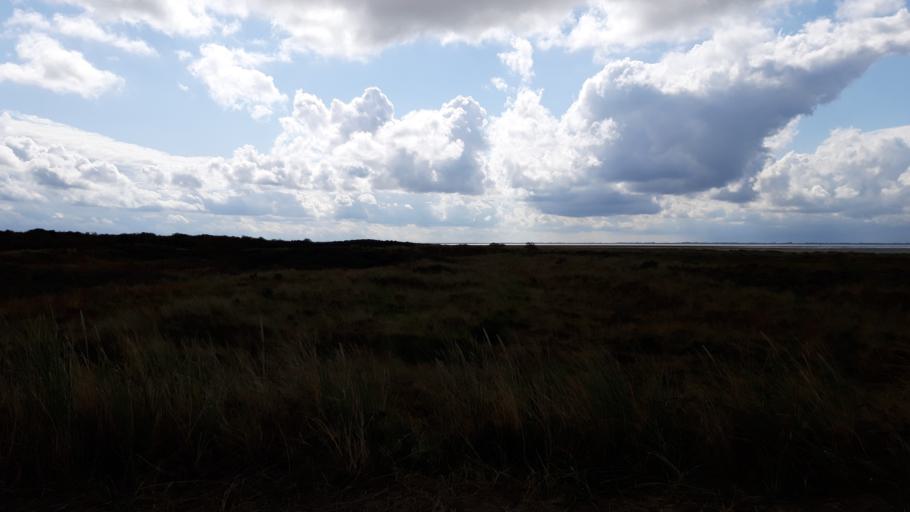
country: NL
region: Friesland
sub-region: Gemeente Schiermonnikoog
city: Schiermonnikoog
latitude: 53.4770
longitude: 6.1343
